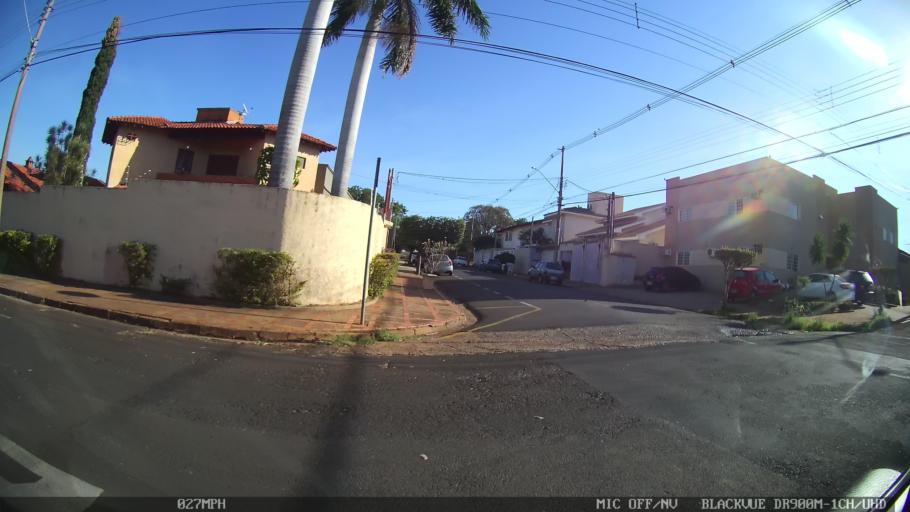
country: BR
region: Sao Paulo
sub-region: Sao Jose Do Rio Preto
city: Sao Jose do Rio Preto
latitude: -20.8229
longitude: -49.4084
